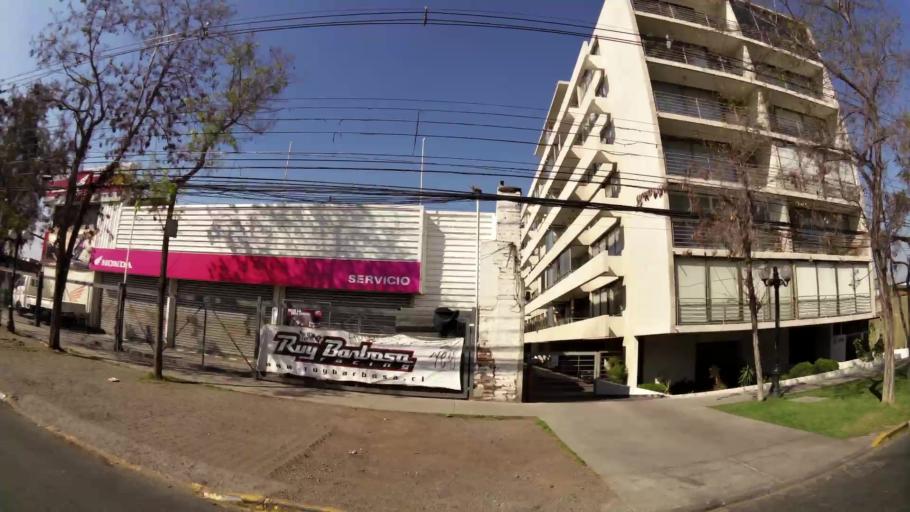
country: CL
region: Santiago Metropolitan
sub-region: Provincia de Santiago
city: Santiago
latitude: -33.4472
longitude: -70.6285
